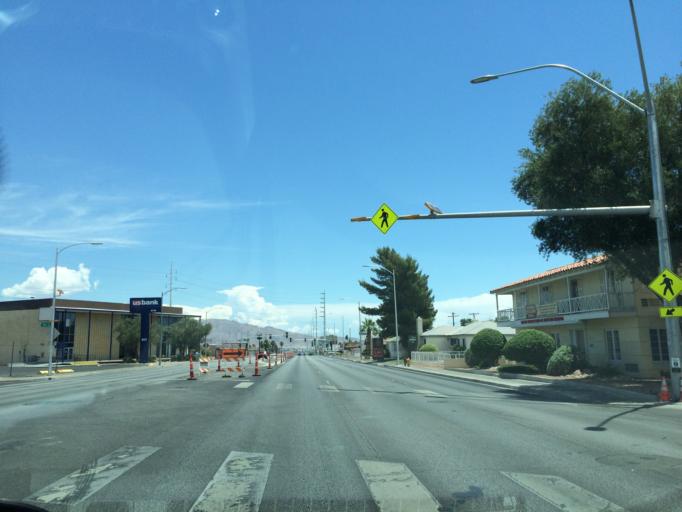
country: US
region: Nevada
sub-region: Clark County
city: Las Vegas
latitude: 36.1588
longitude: -115.1434
